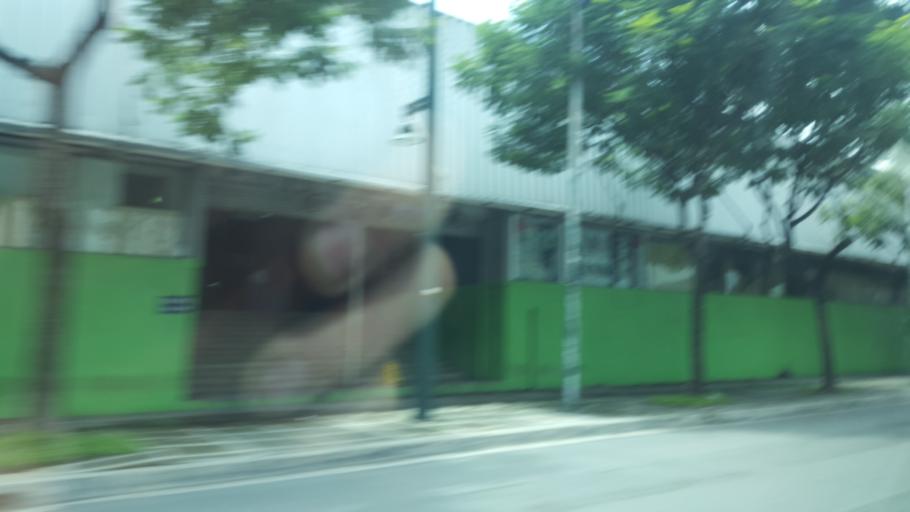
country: PH
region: Metro Manila
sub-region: Makati City
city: Makati City
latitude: 14.5554
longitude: 121.0511
